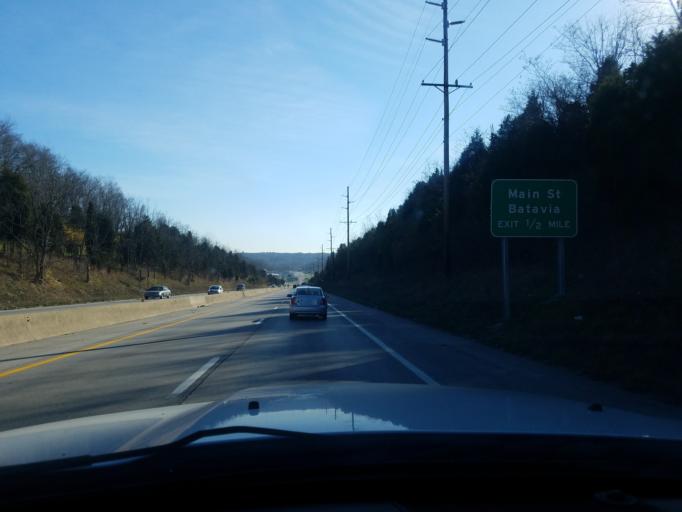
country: US
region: Ohio
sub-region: Clermont County
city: Batavia
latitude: 39.0866
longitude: -84.2024
